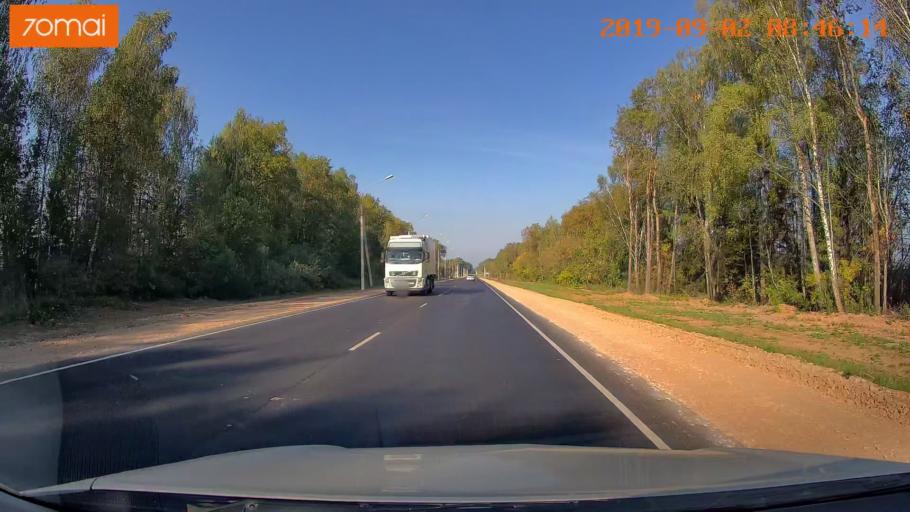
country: RU
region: Kaluga
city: Medyn'
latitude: 54.9689
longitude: 35.9833
